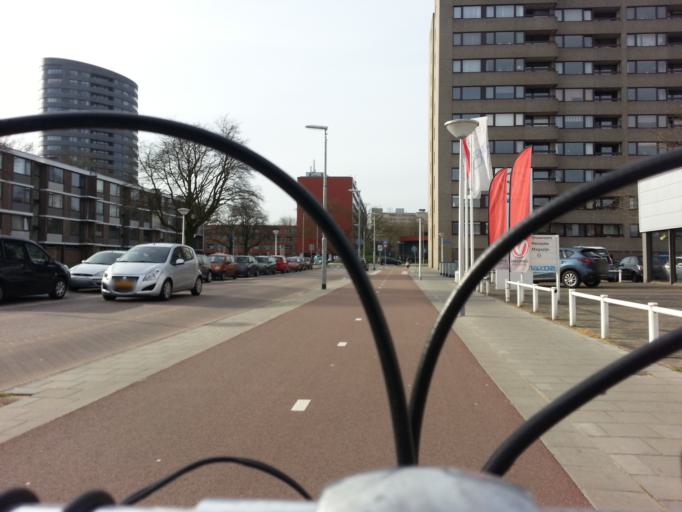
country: NL
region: North Brabant
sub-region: Gemeente Eindhoven
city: Villapark
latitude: 51.4585
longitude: 5.4879
